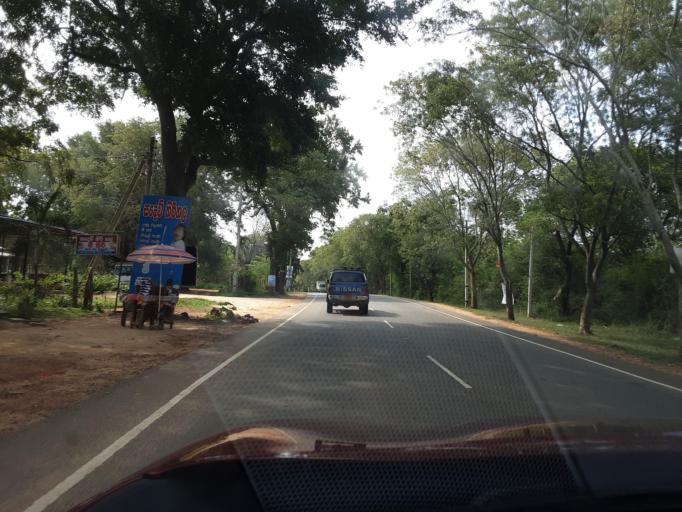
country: LK
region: Uva
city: Haputale
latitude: 6.3630
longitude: 81.1792
